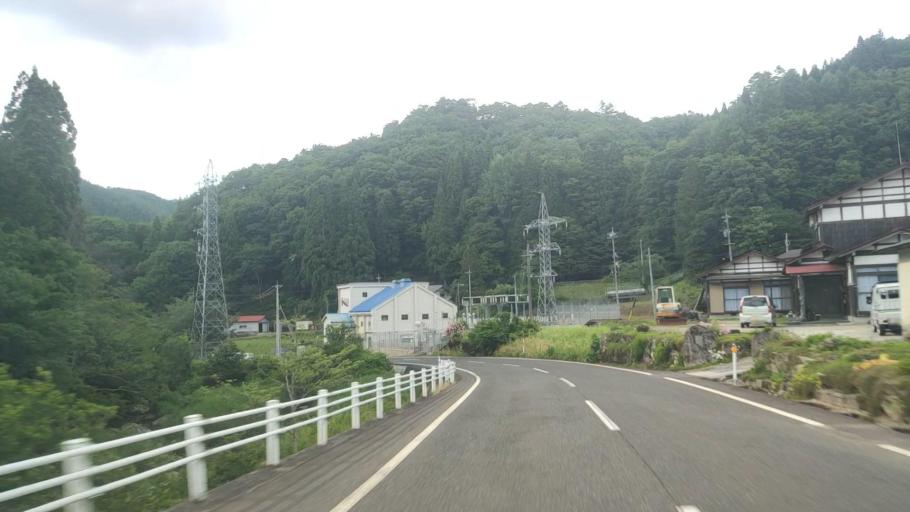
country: JP
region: Tottori
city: Kurayoshi
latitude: 35.2942
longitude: 133.9588
